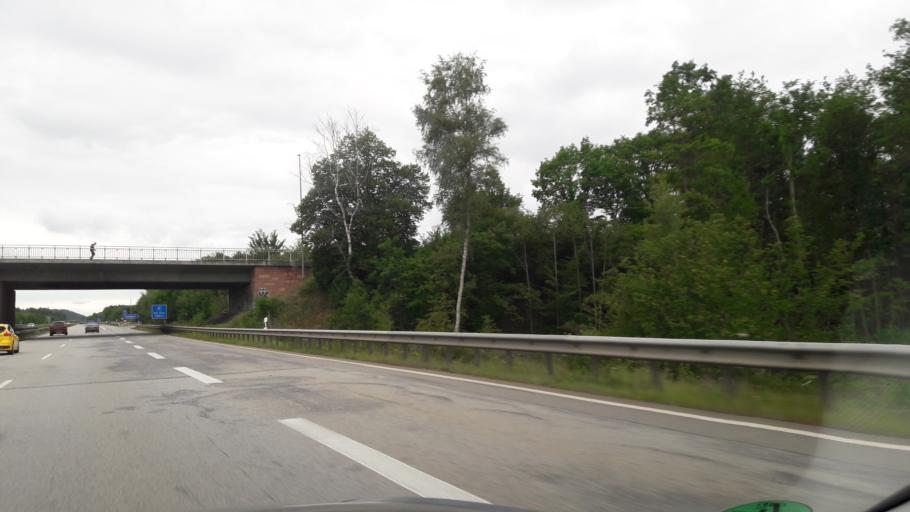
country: DE
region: Rheinland-Pfalz
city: Bruchmuhlbach-Miesau
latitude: 49.3901
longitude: 7.4415
